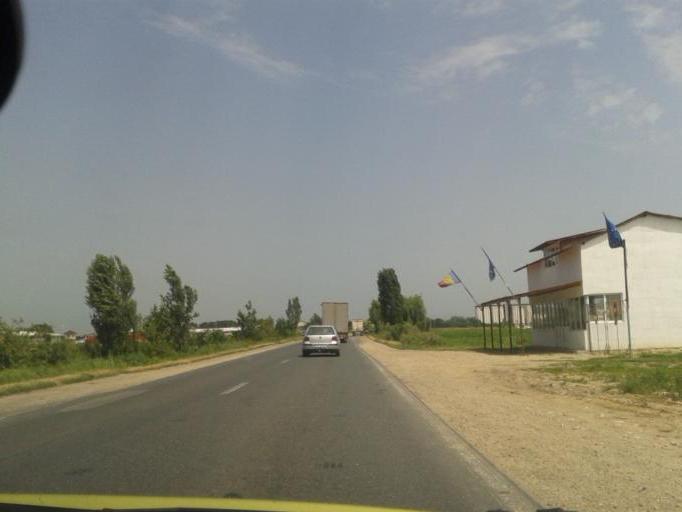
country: RO
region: Dambovita
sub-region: Oras Gaesti
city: Gaesti
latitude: 44.6994
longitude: 25.3115
